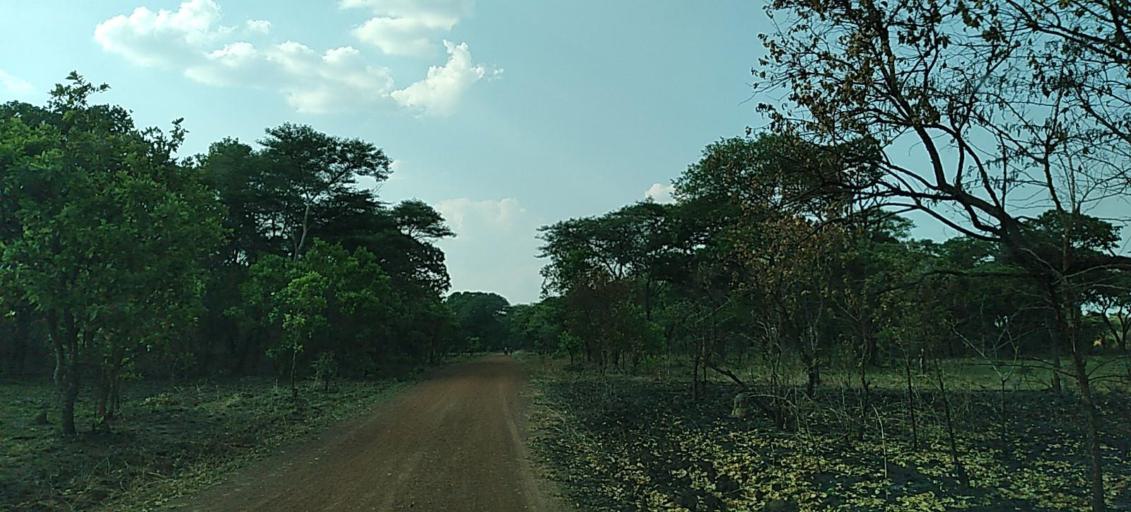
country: ZM
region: Copperbelt
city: Mpongwe
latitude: -13.4361
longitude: 28.0591
